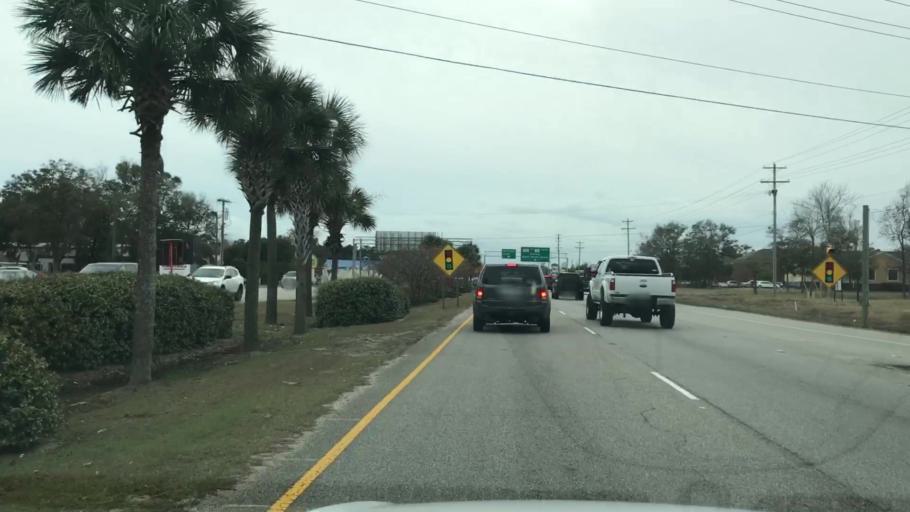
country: US
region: South Carolina
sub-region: Georgetown County
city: Murrells Inlet
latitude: 33.5697
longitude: -79.0325
